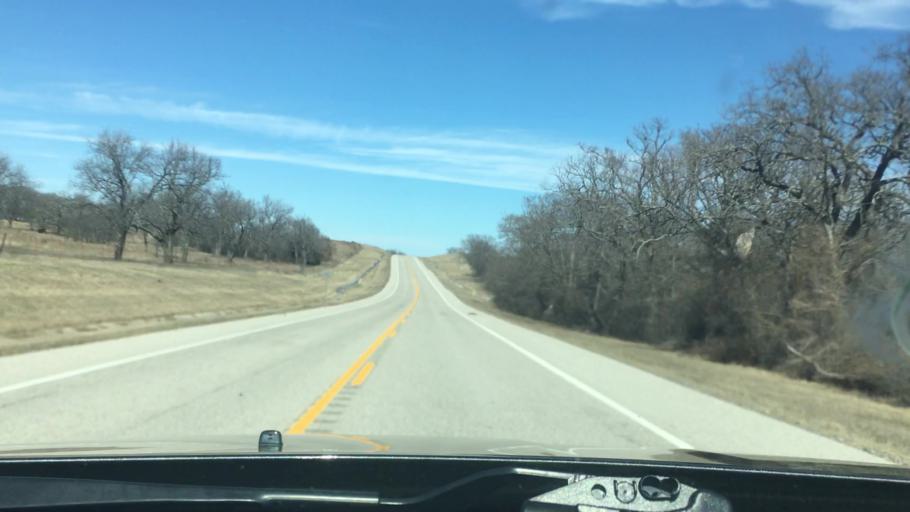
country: US
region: Oklahoma
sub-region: Carter County
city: Dickson
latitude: 34.3368
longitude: -96.9509
